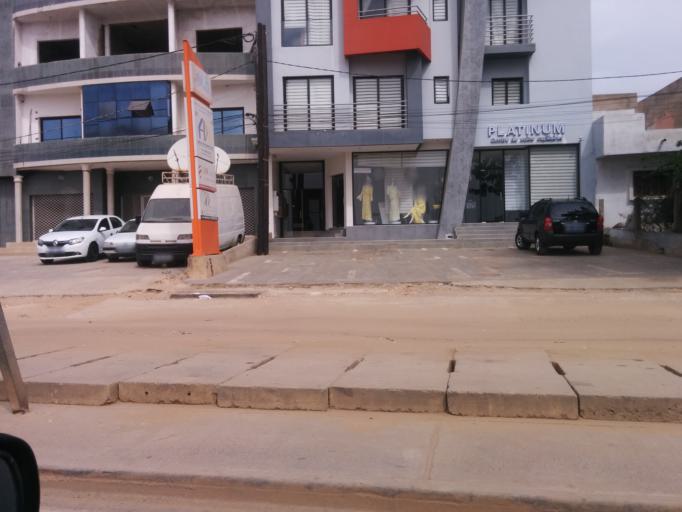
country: SN
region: Dakar
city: Mermoz Boabab
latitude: 14.7260
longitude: -17.4713
